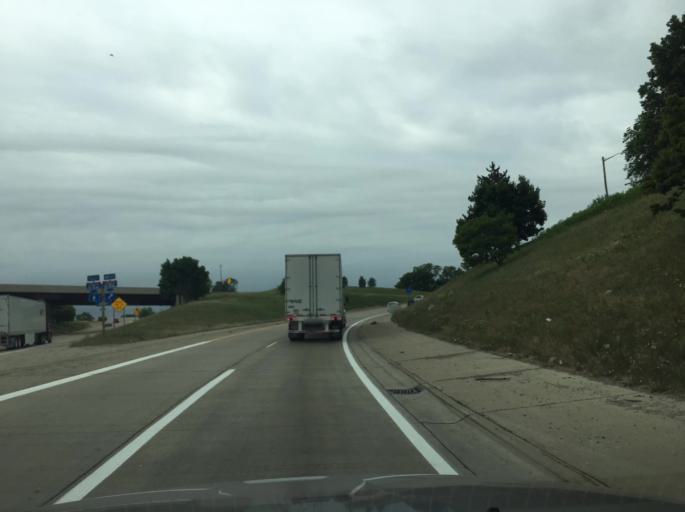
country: US
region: Michigan
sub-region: Macomb County
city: Center Line
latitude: 42.4904
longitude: -83.0468
